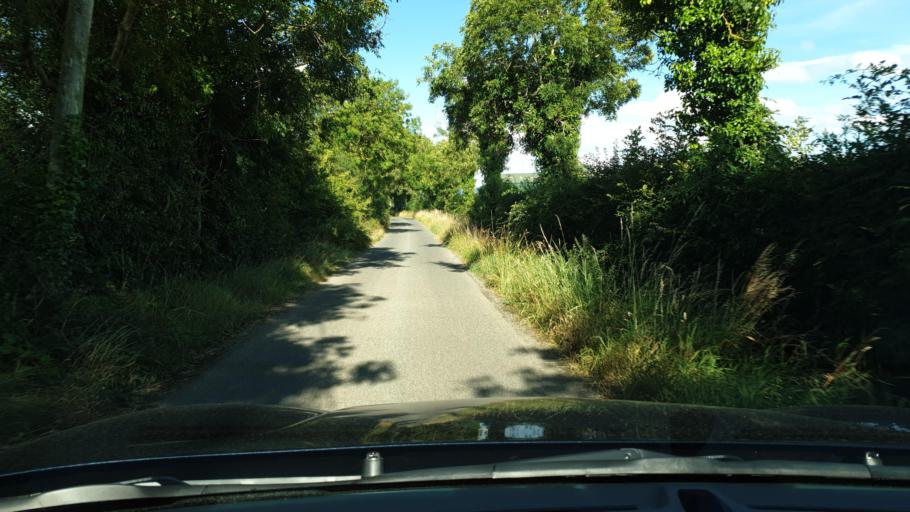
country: IE
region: Leinster
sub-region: An Mhi
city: Ashbourne
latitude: 53.5241
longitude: -6.3827
